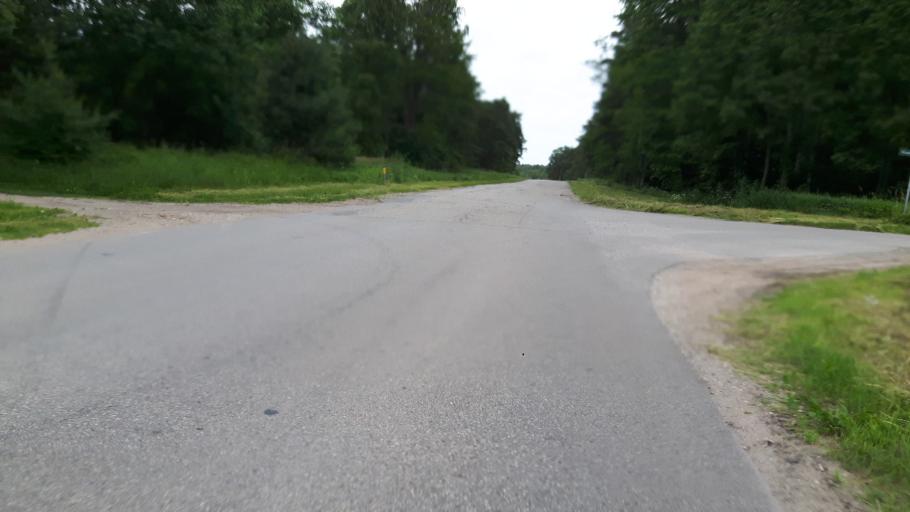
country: LV
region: Liepaja
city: Vec-Liepaja
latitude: 56.5847
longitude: 21.0268
